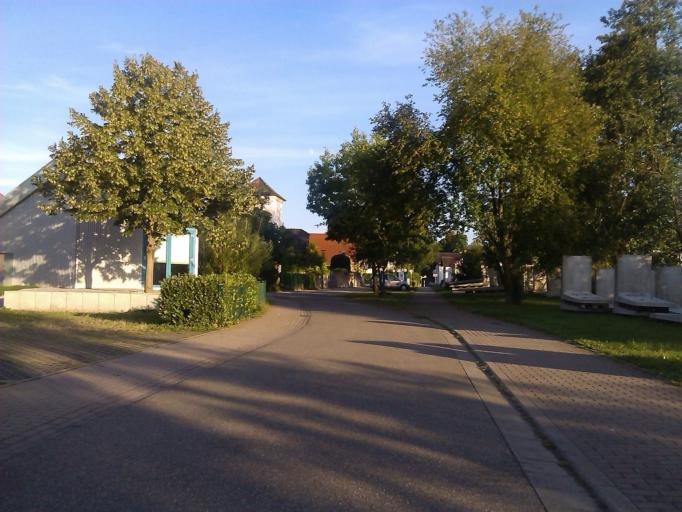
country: DE
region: Baden-Wuerttemberg
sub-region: Karlsruhe Region
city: Rauenberg
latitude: 49.2593
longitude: 8.7129
